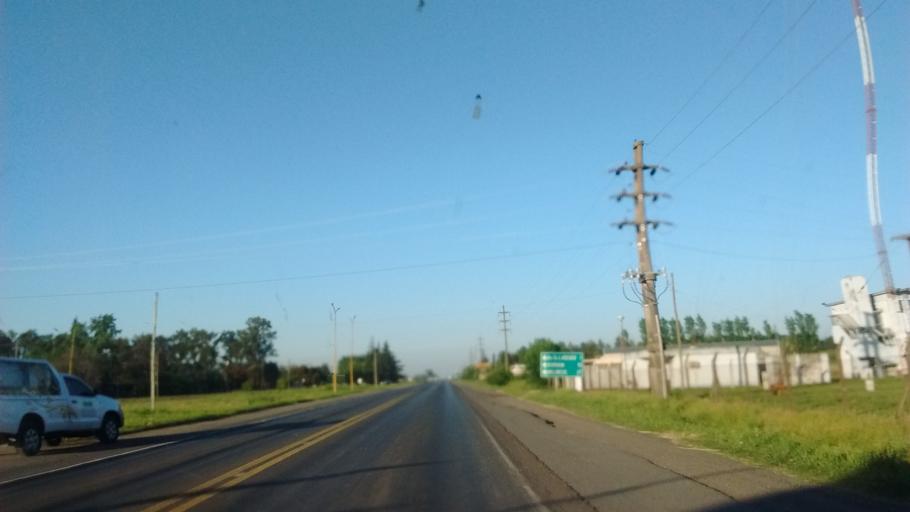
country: AR
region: Santa Fe
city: Firmat
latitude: -33.4558
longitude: -61.5022
